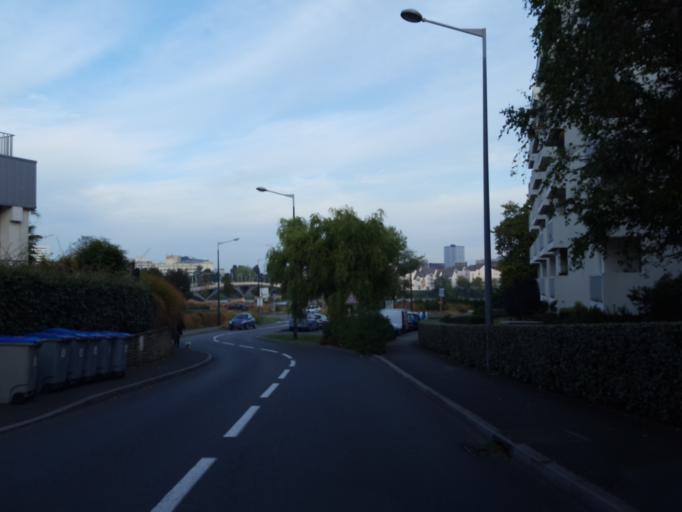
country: FR
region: Pays de la Loire
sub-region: Departement de la Loire-Atlantique
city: Saint-Sebastien-sur-Loire
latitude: 47.2045
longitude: -1.5217
